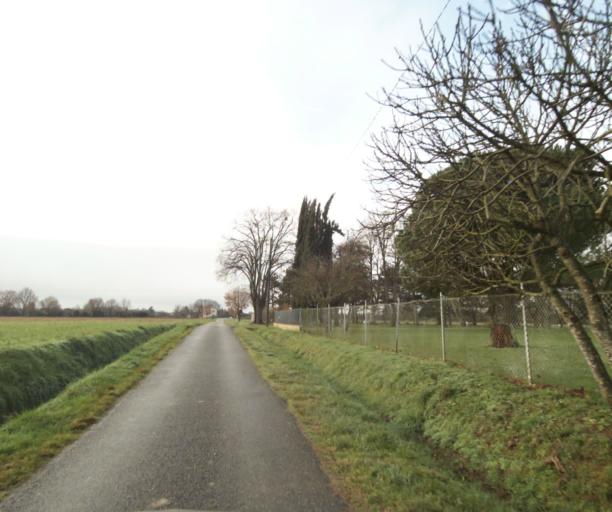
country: FR
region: Midi-Pyrenees
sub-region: Departement de la Haute-Garonne
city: Villemur-sur-Tarn
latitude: 43.8762
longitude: 1.4843
